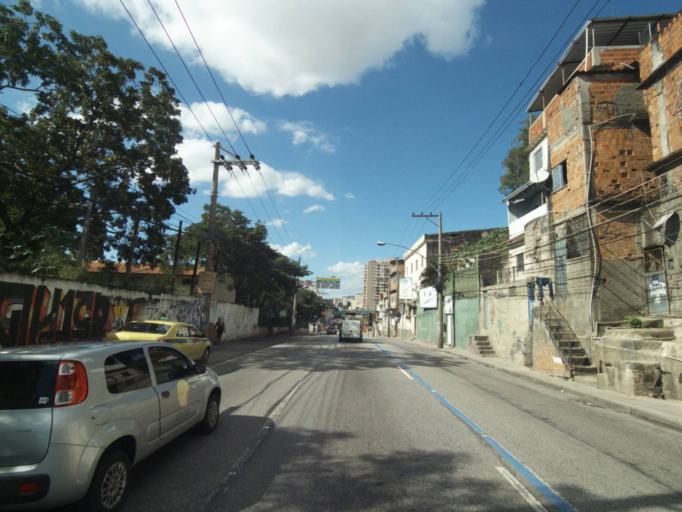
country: BR
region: Rio de Janeiro
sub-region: Rio De Janeiro
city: Rio de Janeiro
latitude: -22.9040
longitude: -43.2623
